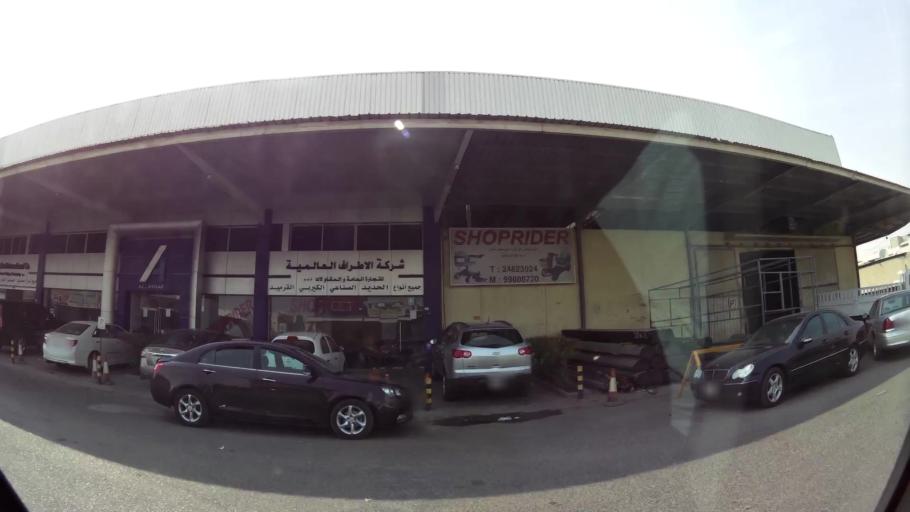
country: KW
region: Al Asimah
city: Ar Rabiyah
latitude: 29.3195
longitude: 47.9350
